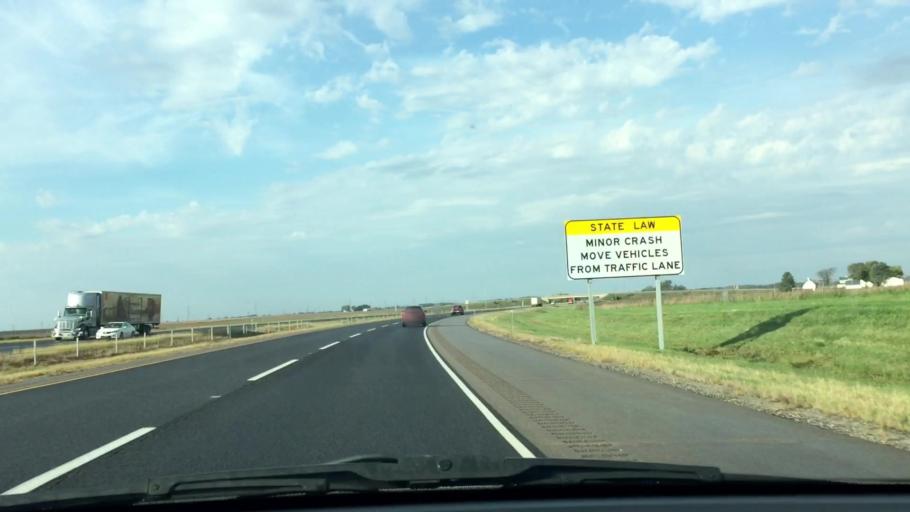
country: US
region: Illinois
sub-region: Lee County
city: Dixon
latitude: 41.7818
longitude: -89.5437
